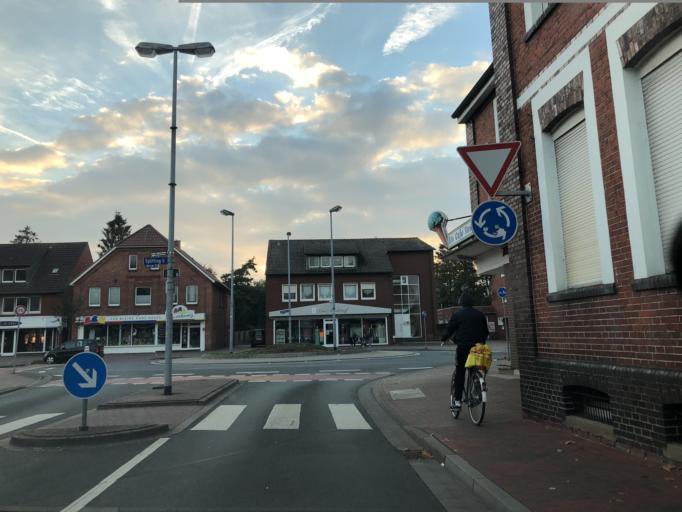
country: DE
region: Lower Saxony
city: Papenburg
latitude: 53.0748
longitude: 7.4417
